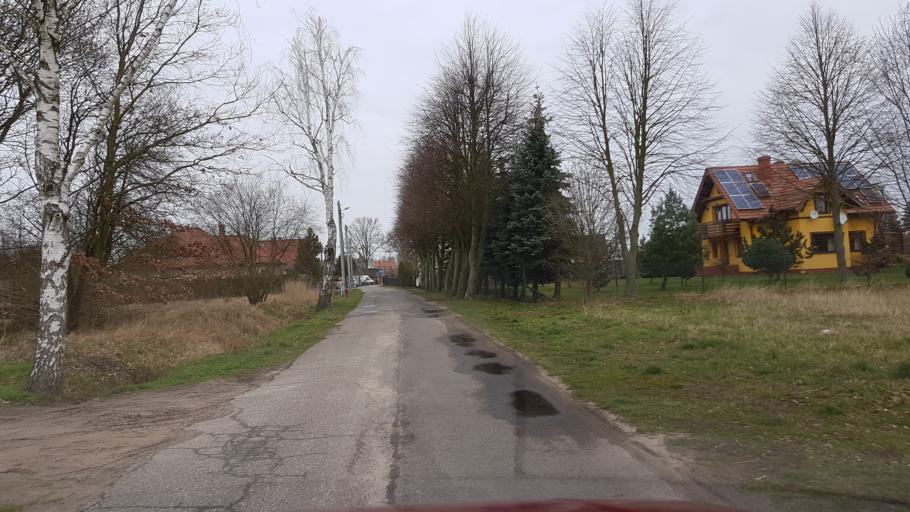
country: PL
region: West Pomeranian Voivodeship
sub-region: Powiat goleniowski
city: Stepnica
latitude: 53.6534
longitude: 14.5145
